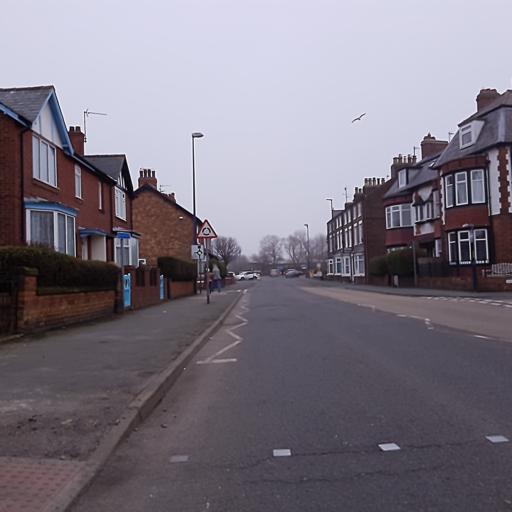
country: GB
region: England
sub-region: North Yorkshire
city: Filey
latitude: 54.2111
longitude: -0.2908
